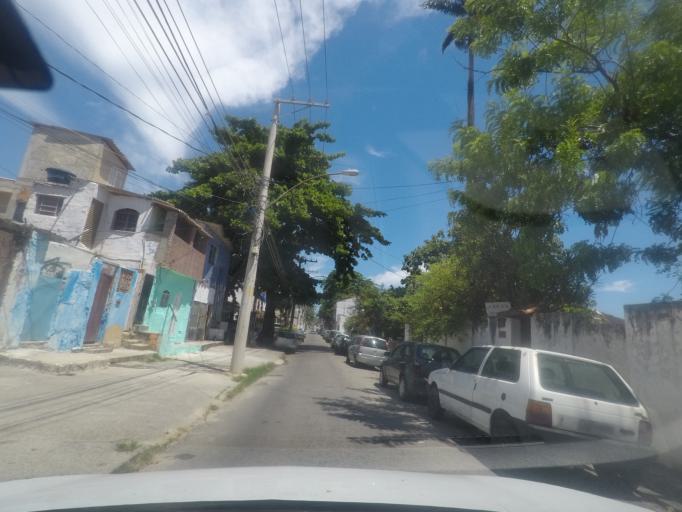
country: BR
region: Rio de Janeiro
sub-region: Itaguai
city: Itaguai
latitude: -23.0009
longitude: -43.6427
